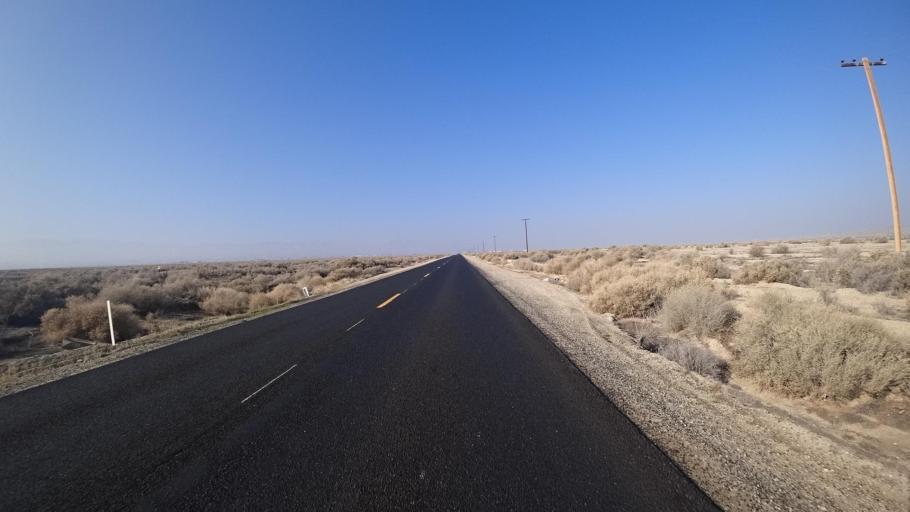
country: US
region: California
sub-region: Kern County
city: Ford City
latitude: 35.1805
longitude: -119.4936
